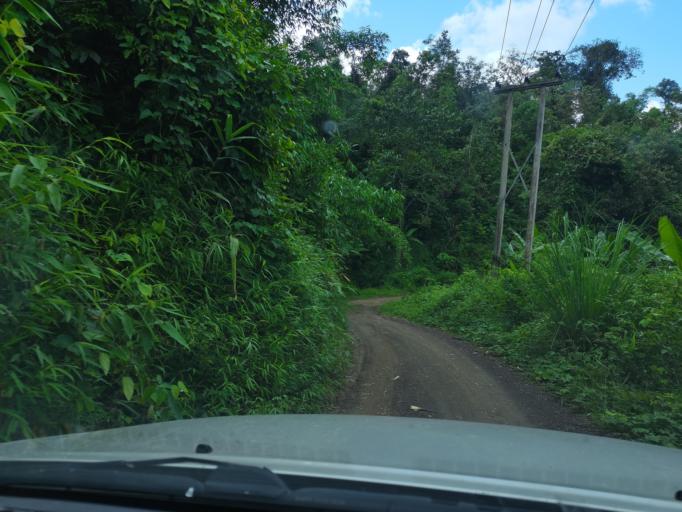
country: LA
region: Loungnamtha
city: Muang Long
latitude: 20.7672
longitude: 101.0179
